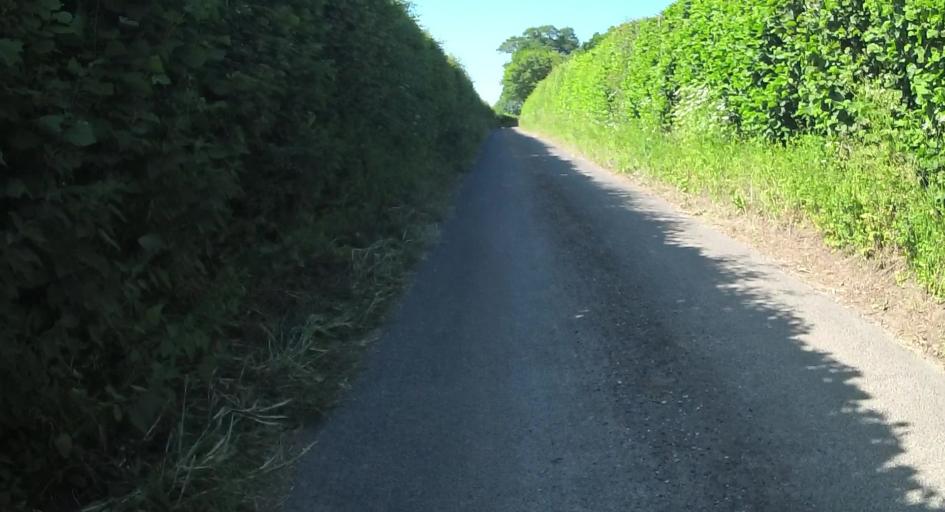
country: GB
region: England
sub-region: Hampshire
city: Overton
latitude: 51.2384
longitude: -1.3108
